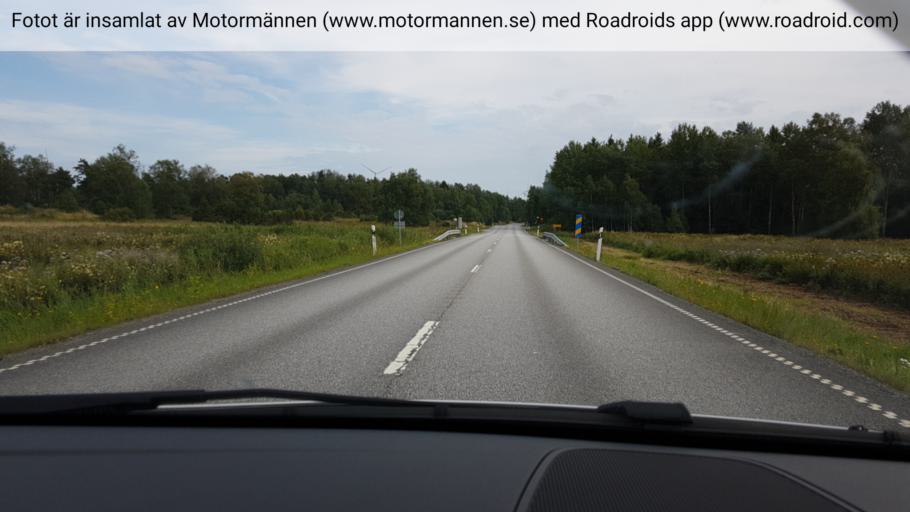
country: SE
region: Stockholm
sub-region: Norrtalje Kommun
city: Hallstavik
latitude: 60.0805
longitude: 18.5101
